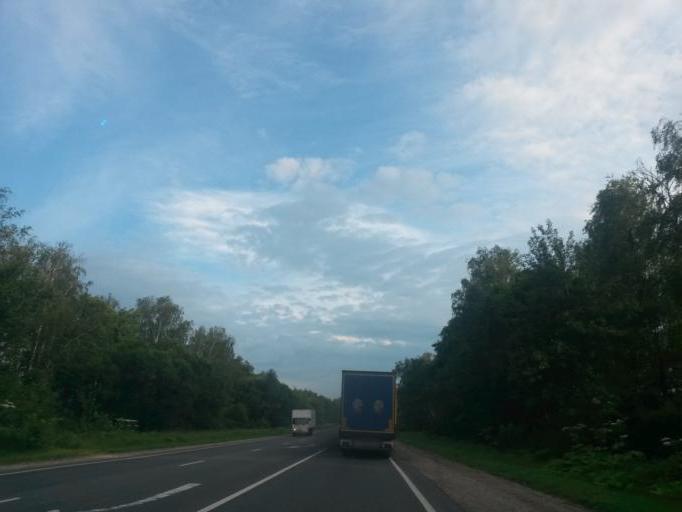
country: RU
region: Moskovskaya
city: Barybino
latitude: 55.2248
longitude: 37.8673
